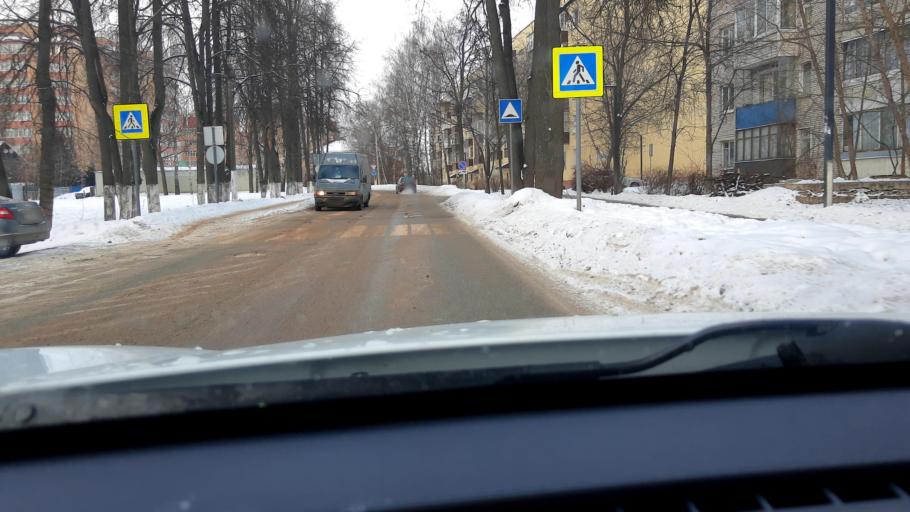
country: RU
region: Moskovskaya
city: Pavlovskaya Sloboda
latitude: 55.8163
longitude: 37.0866
